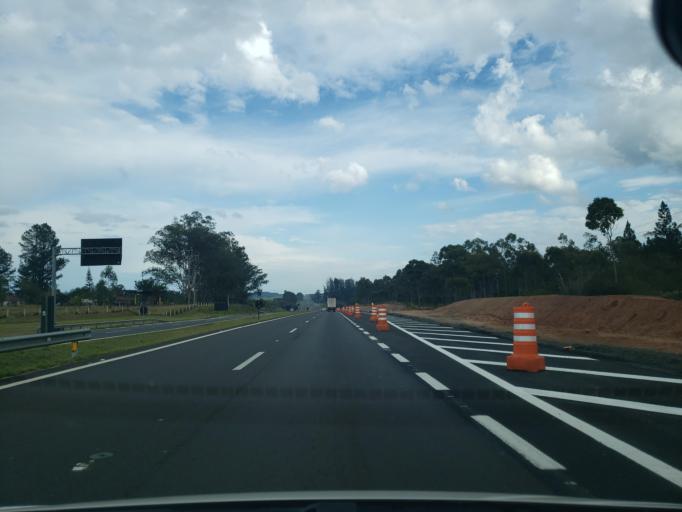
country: BR
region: Sao Paulo
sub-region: Itirapina
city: Itirapina
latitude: -22.2639
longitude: -47.9047
